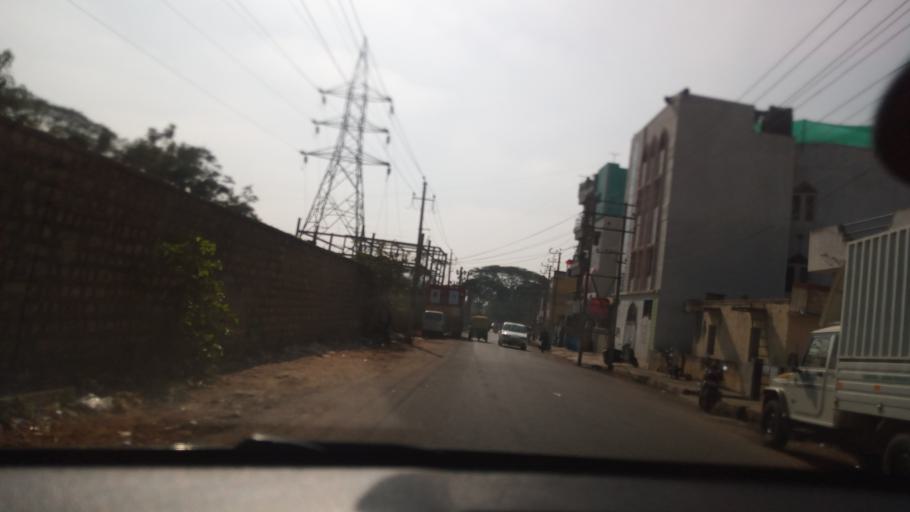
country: IN
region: Karnataka
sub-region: Bangalore Urban
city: Yelahanka
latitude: 13.0447
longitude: 77.5530
